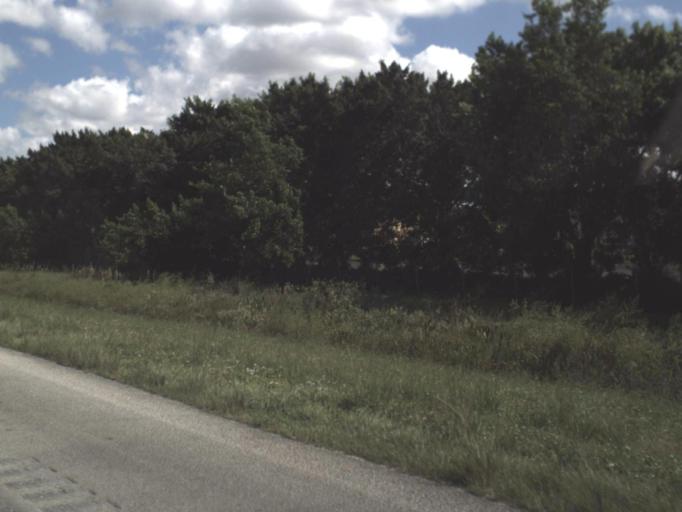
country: US
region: Florida
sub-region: Miami-Dade County
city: Country Club
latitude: 25.9604
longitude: -80.3370
